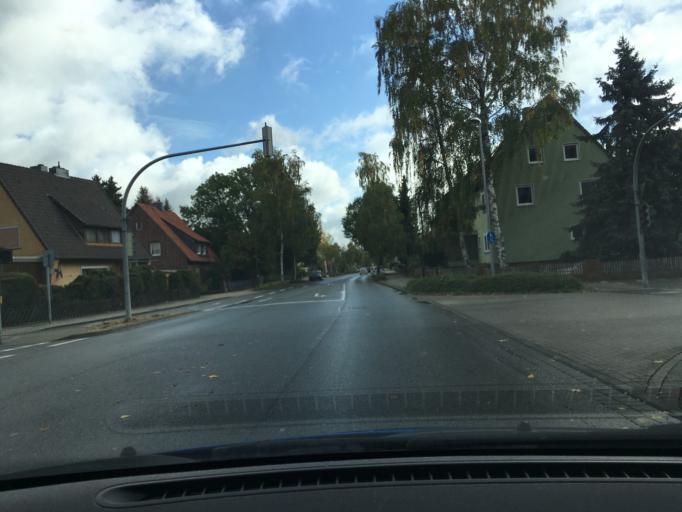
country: DE
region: Lower Saxony
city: Uelzen
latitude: 52.9736
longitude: 10.5651
